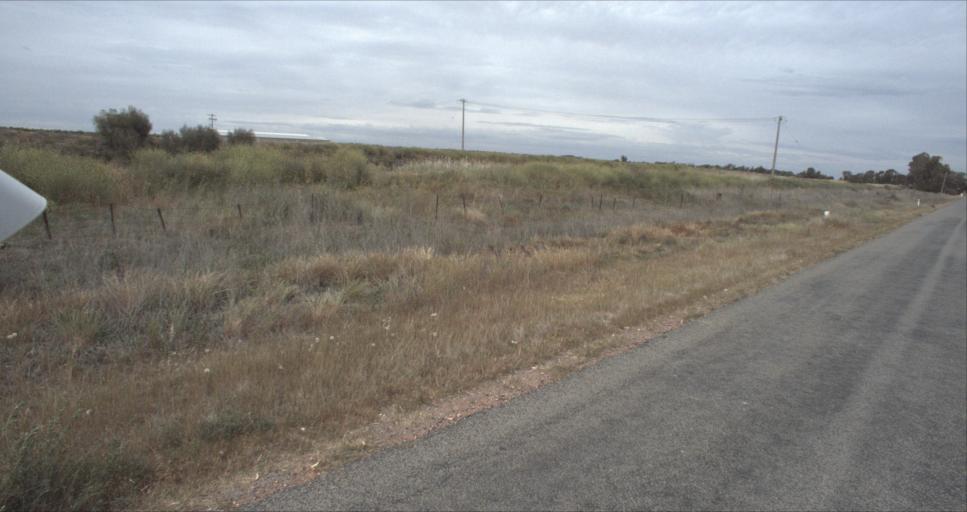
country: AU
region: New South Wales
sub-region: Leeton
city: Leeton
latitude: -34.4380
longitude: 146.3761
